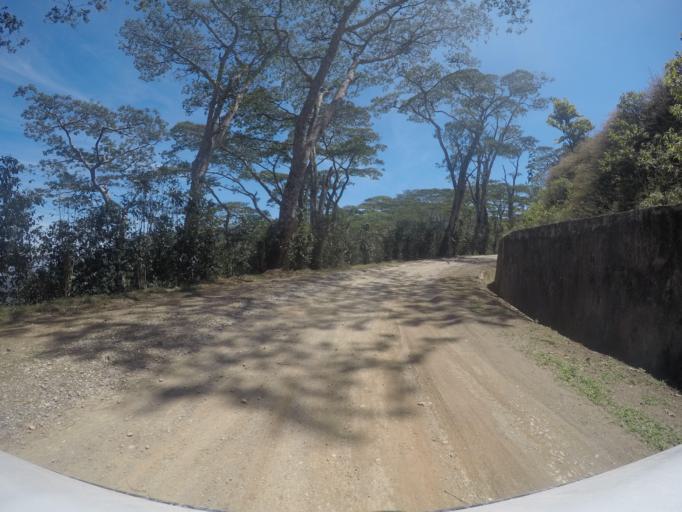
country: TL
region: Ermera
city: Gleno
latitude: -8.7843
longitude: 125.3744
